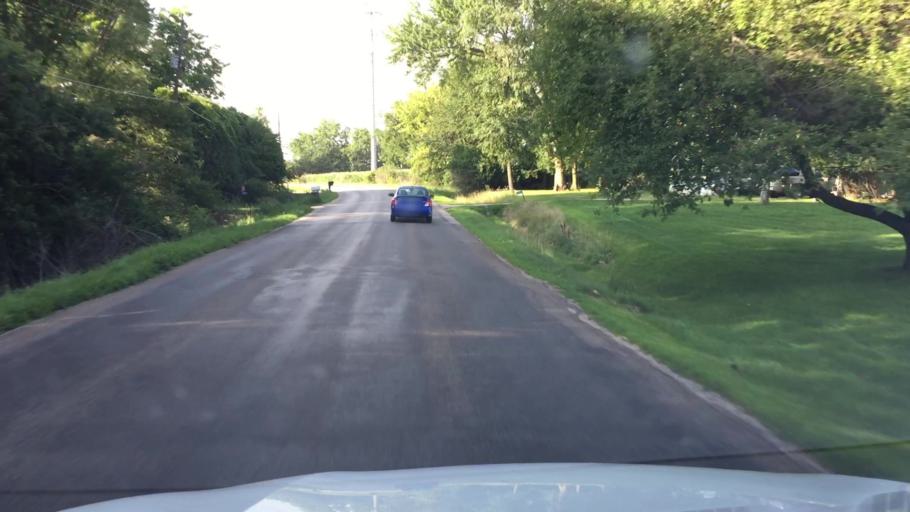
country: US
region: Iowa
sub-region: Linn County
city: Ely
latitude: 41.8254
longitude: -91.6237
